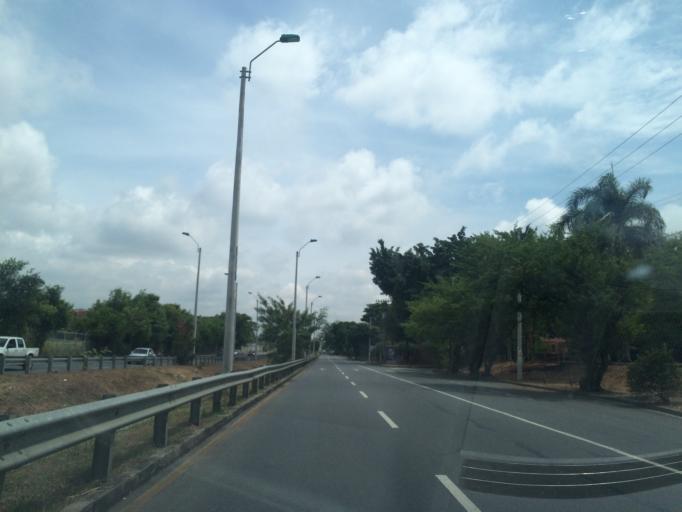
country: CO
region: Valle del Cauca
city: Cali
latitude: 3.3742
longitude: -76.5292
